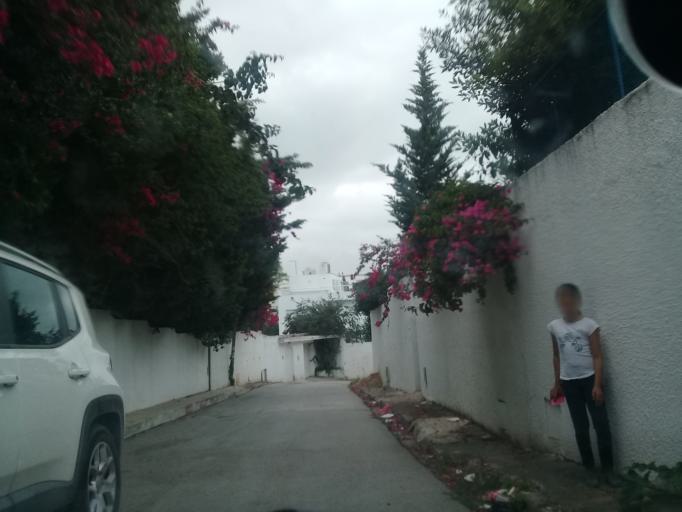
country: TN
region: Tunis
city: Sidi Bou Said
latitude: 36.8700
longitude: 10.3398
